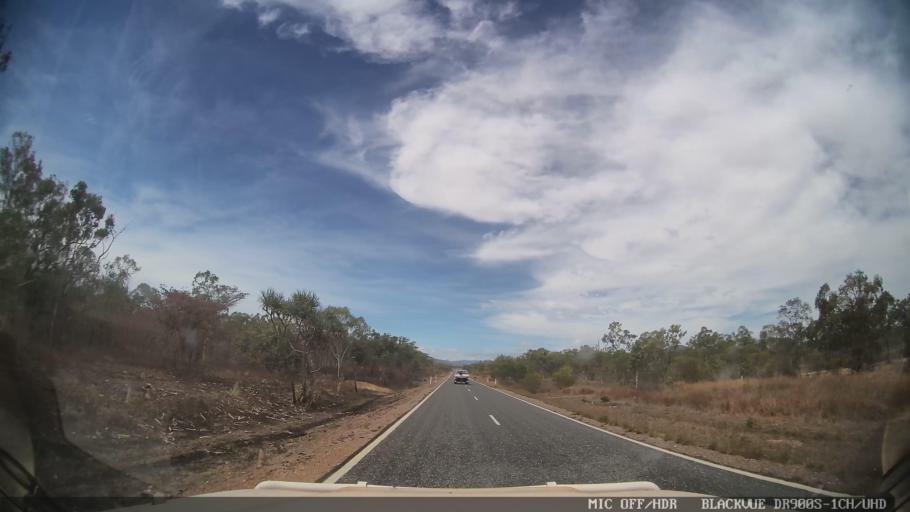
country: AU
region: Queensland
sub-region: Cairns
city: Port Douglas
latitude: -16.5106
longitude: 145.0566
